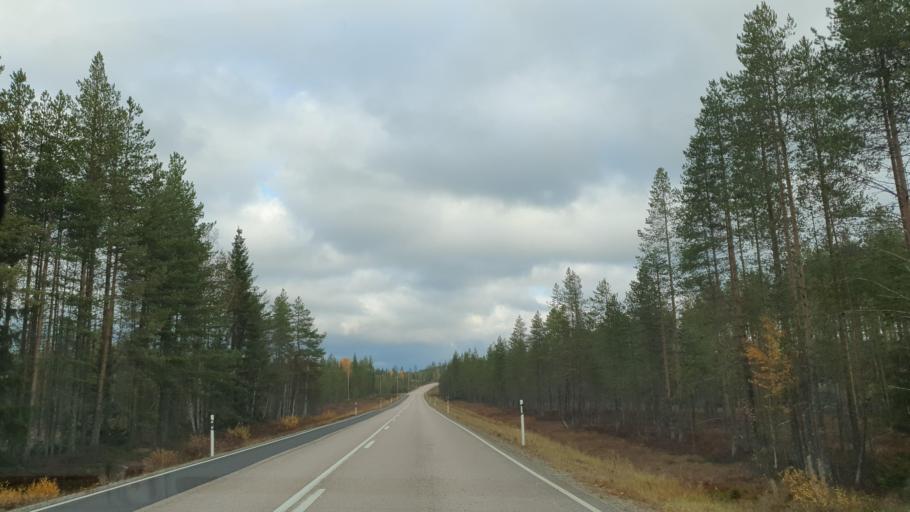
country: FI
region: Kainuu
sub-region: Kehys-Kainuu
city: Kuhmo
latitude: 64.4604
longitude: 29.5535
